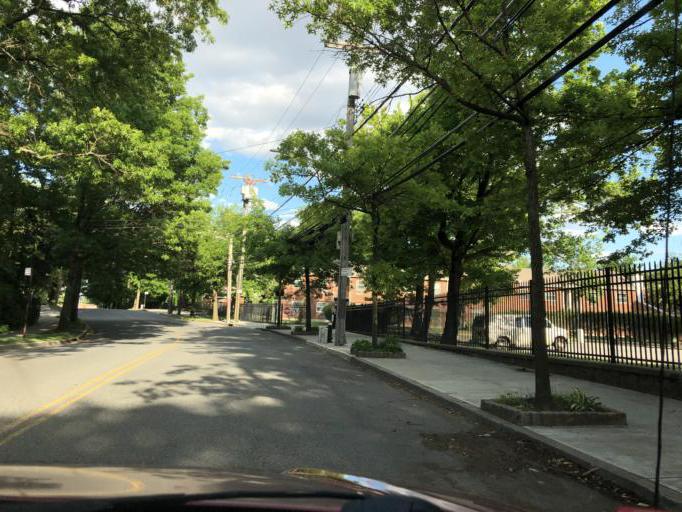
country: US
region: New York
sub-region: Richmond County
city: Staten Island
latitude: 40.5962
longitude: -74.0903
